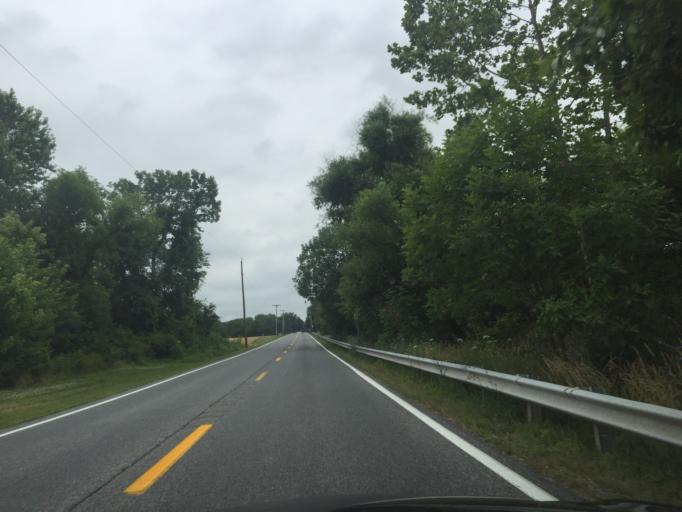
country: US
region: Maryland
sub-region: Harford County
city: Jarrettsville
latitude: 39.5577
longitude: -76.5249
